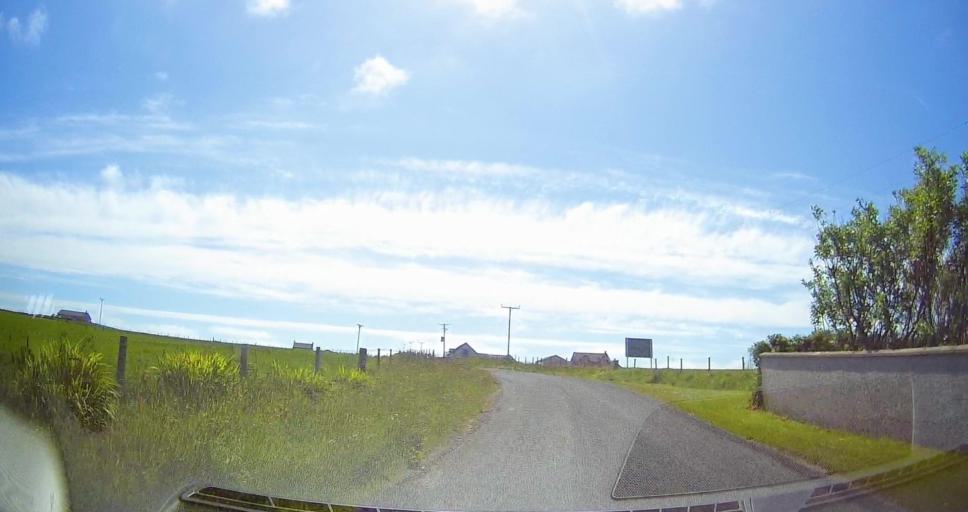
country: GB
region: Scotland
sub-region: Orkney Islands
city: Kirkwall
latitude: 58.8360
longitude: -2.9188
